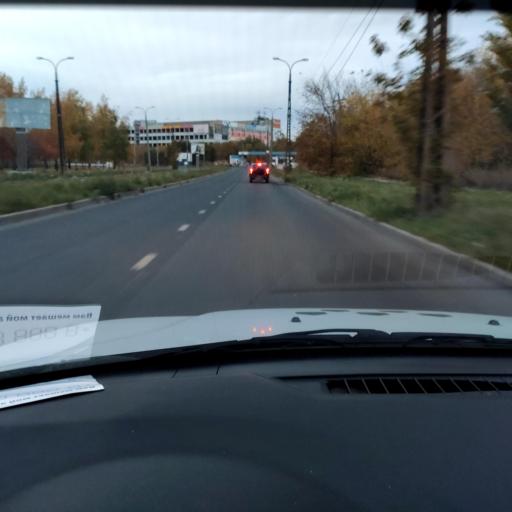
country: RU
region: Samara
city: Tol'yatti
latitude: 53.5582
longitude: 49.3047
